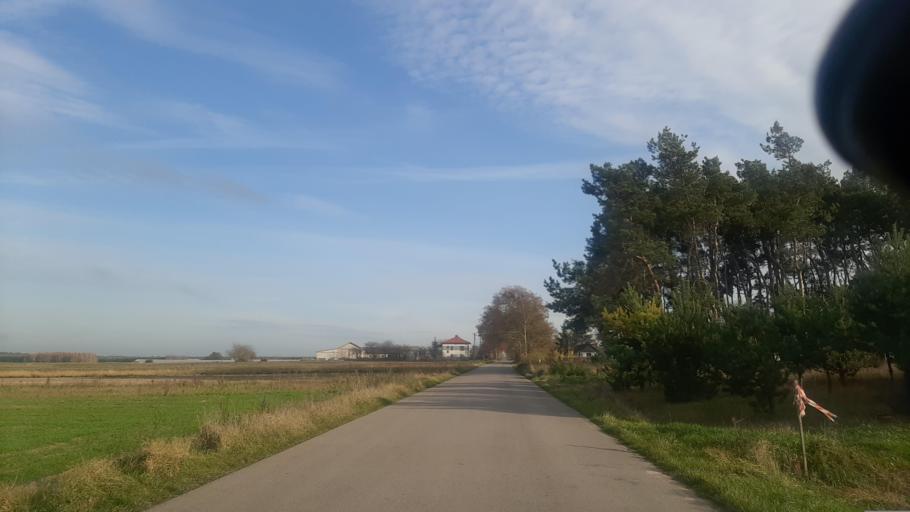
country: PL
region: Lublin Voivodeship
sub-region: Powiat lubelski
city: Garbow
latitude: 51.3974
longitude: 22.3384
